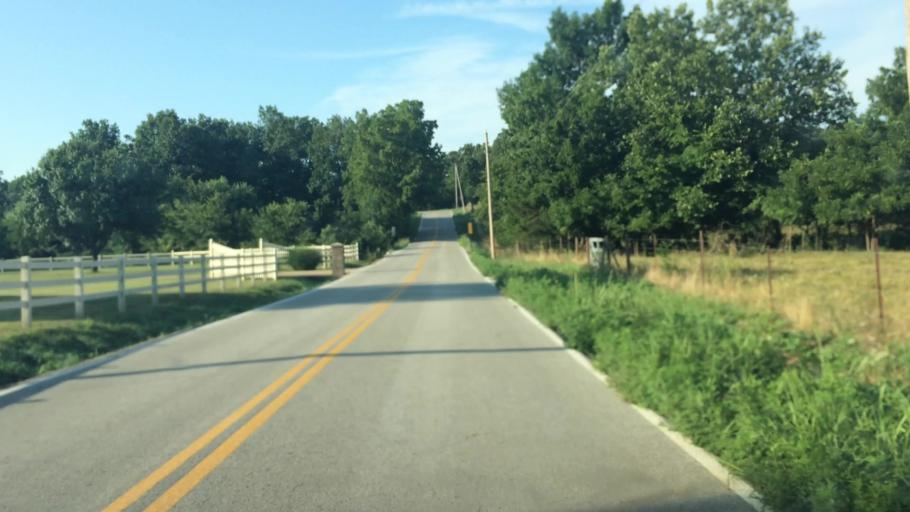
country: US
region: Missouri
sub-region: Greene County
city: Strafford
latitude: 37.2578
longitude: -93.1878
